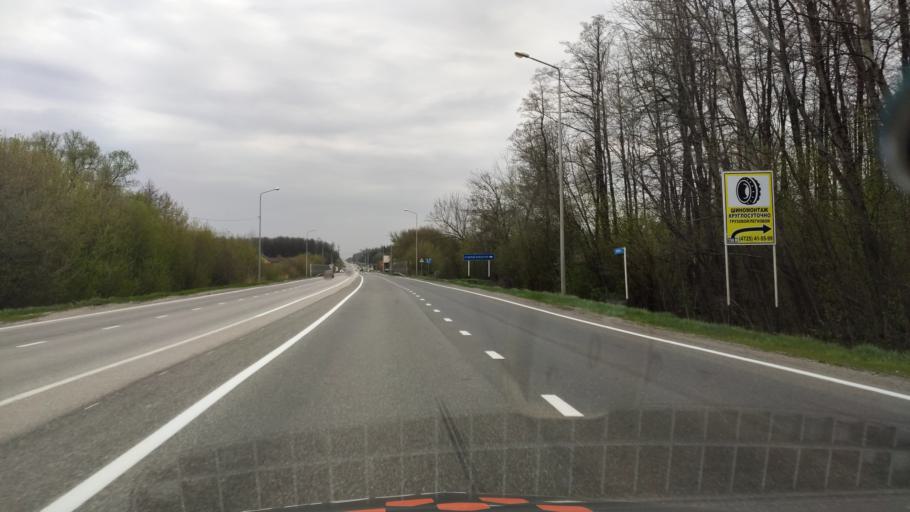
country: RU
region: Belgorod
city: Staryy Oskol
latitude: 51.3517
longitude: 37.8288
